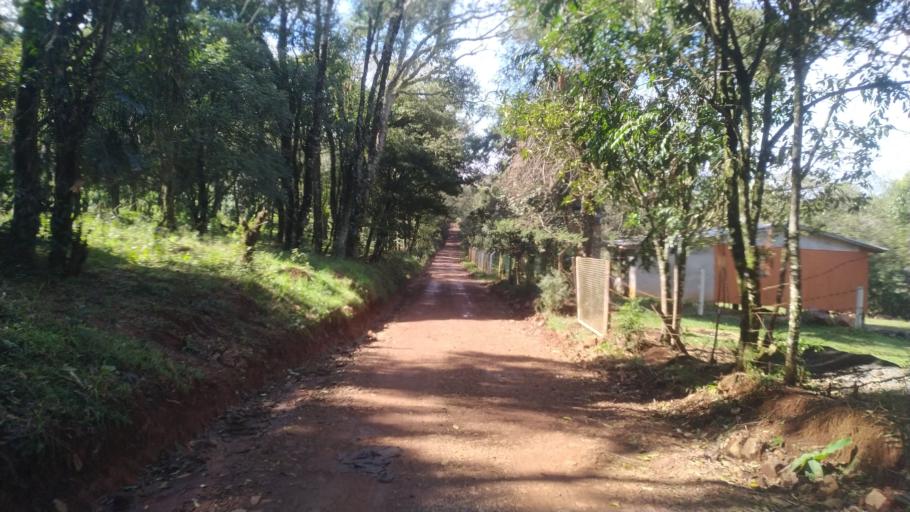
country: BR
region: Santa Catarina
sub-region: Chapeco
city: Chapeco
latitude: -27.1618
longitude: -52.6036
